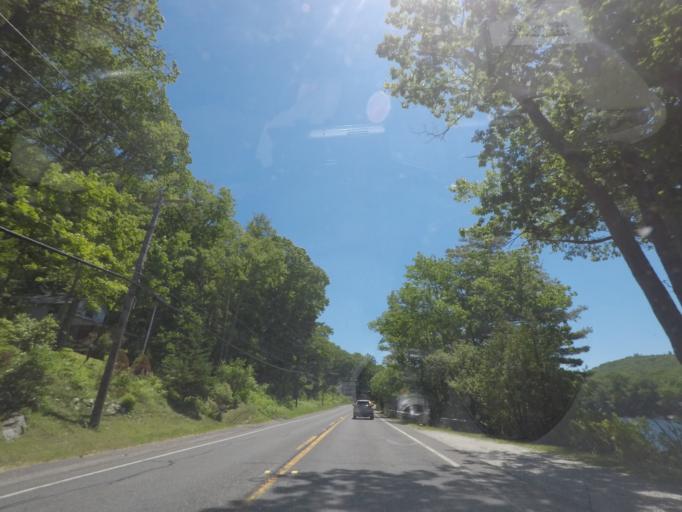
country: US
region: Massachusetts
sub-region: Berkshire County
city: Becket
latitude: 42.2840
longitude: -73.1449
